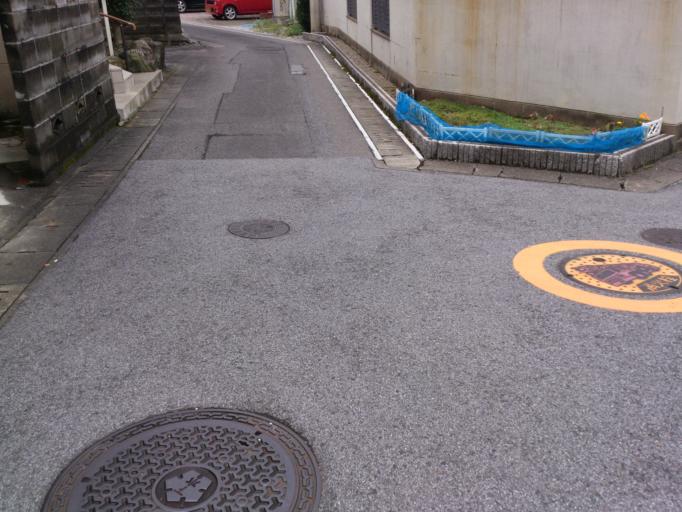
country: JP
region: Gifu
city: Ogaki
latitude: 35.3701
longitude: 136.6208
